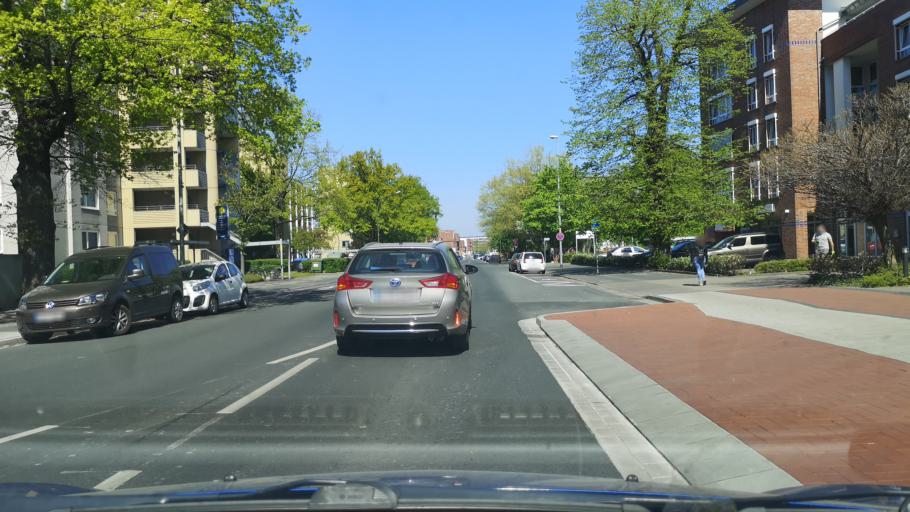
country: DE
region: Lower Saxony
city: Langenhagen
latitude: 52.4421
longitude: 9.7365
